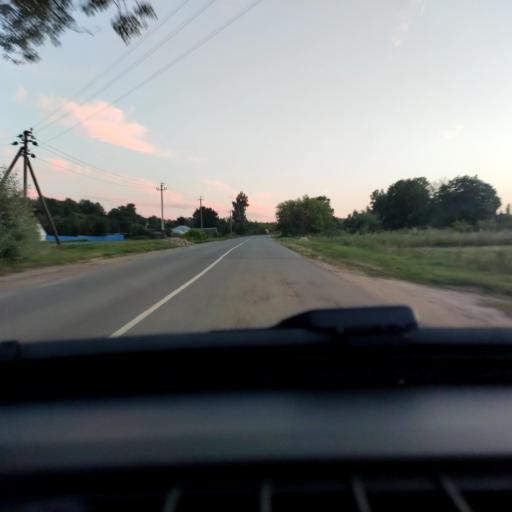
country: RU
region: Lipetsk
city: Zadonsk
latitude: 52.2908
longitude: 38.7597
